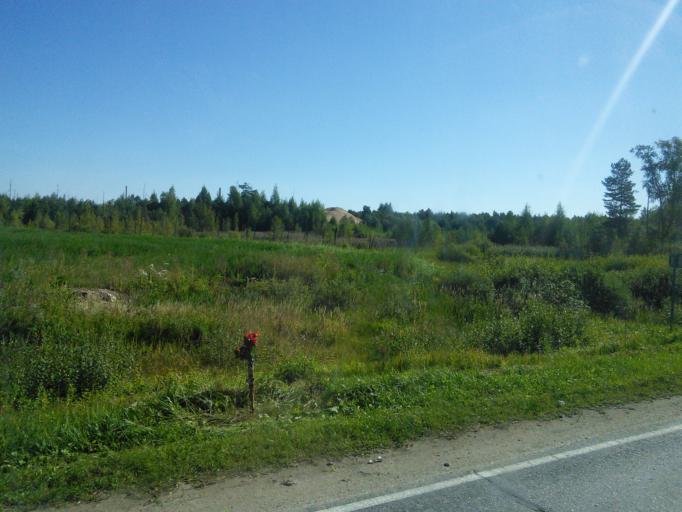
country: RU
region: Jaroslavl
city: Uglich
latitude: 57.4880
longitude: 38.3559
